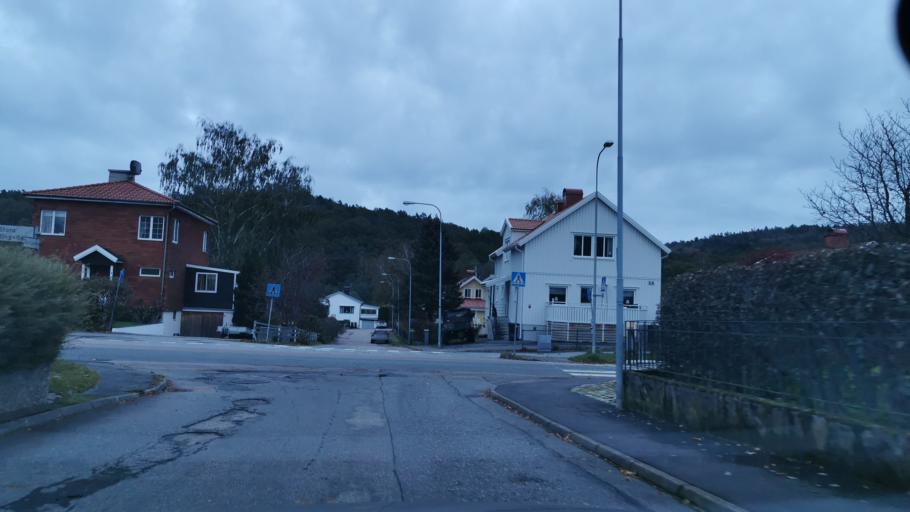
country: SE
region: Vaestra Goetaland
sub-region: Partille Kommun
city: Partille
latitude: 57.7278
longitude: 12.0903
